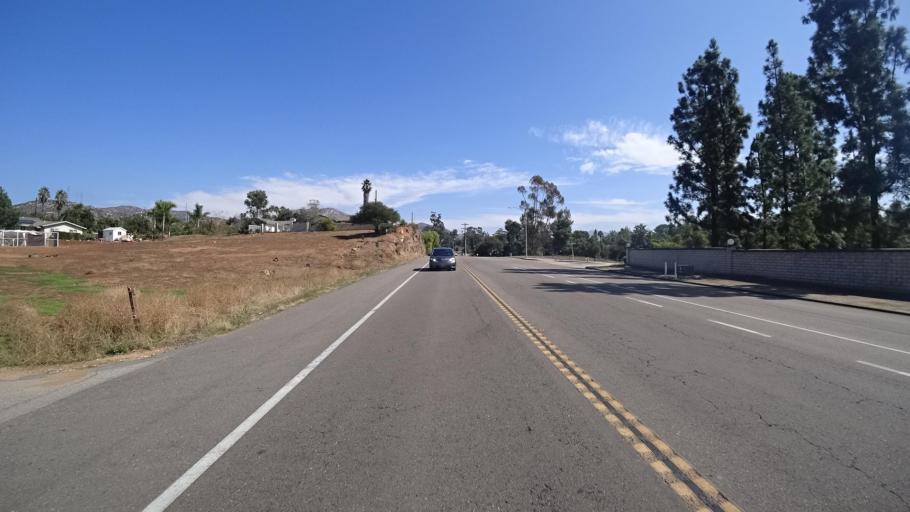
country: US
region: California
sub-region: San Diego County
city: Granite Hills
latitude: 32.7877
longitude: -116.9003
